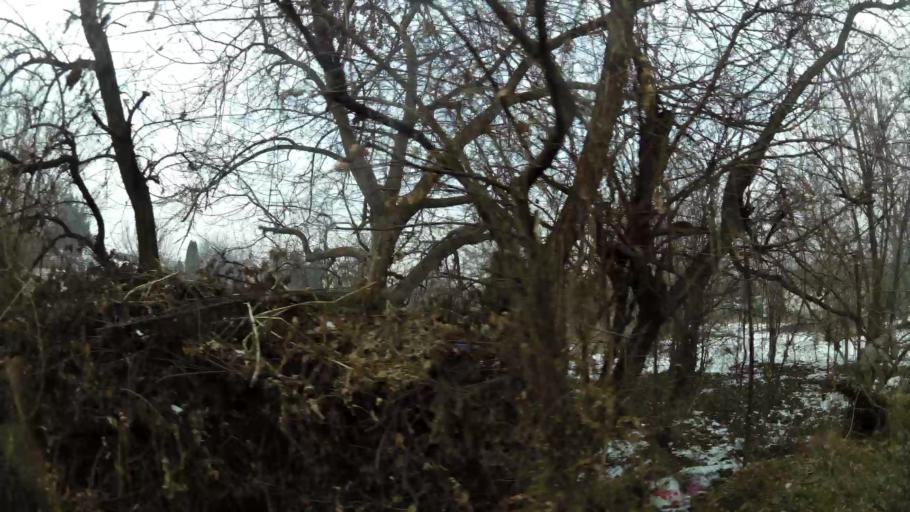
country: MK
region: Cair
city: Cair
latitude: 41.9951
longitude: 21.4609
